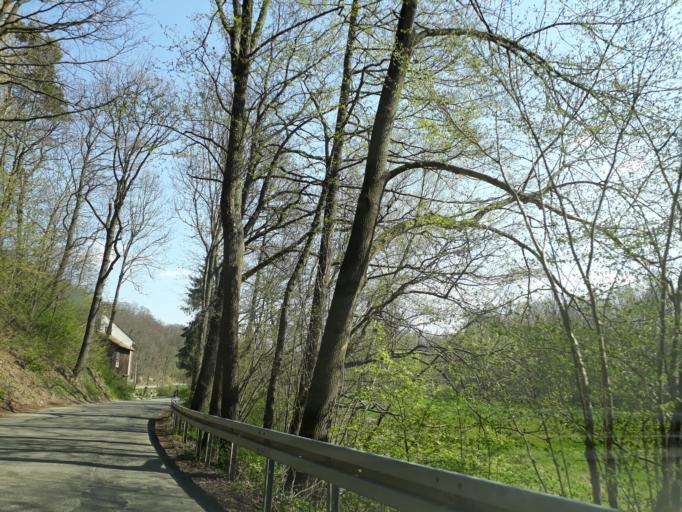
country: DE
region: Saxony
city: Niederschona
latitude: 51.0199
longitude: 13.4665
